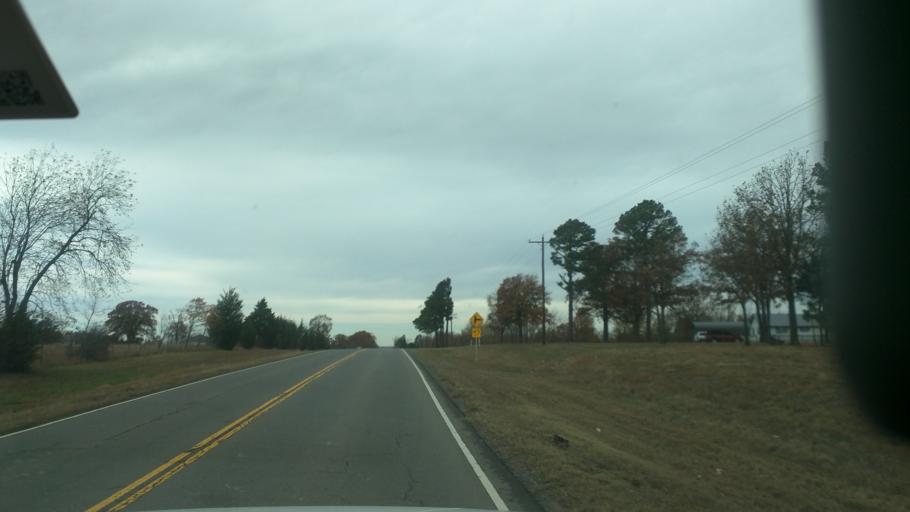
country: US
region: Oklahoma
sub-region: Cherokee County
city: Park Hill
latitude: 35.8991
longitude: -94.8008
